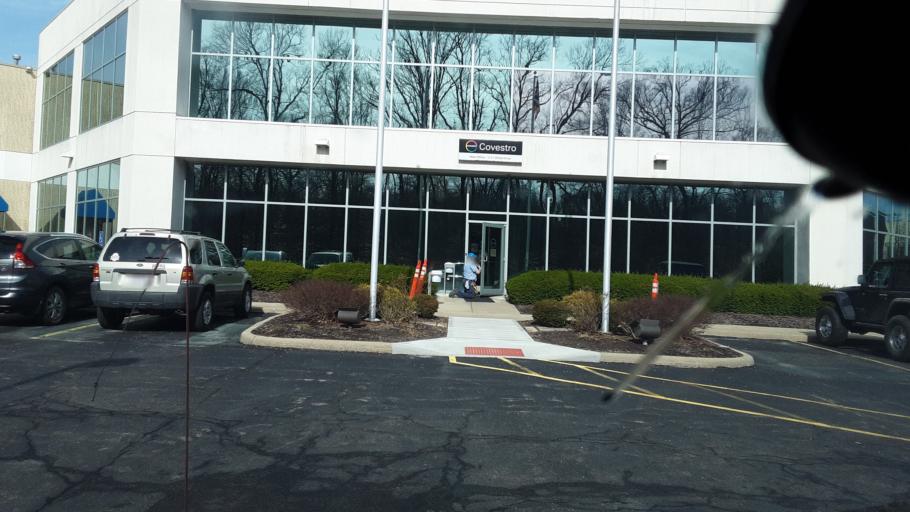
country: US
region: Ohio
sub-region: Licking County
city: Hebron
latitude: 39.9713
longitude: -82.4743
